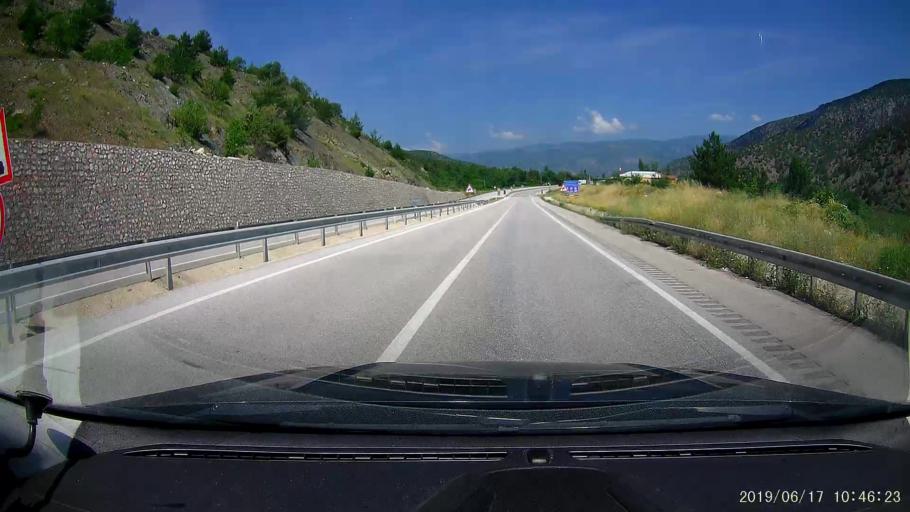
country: TR
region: Corum
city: Hacihamza
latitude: 41.0671
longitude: 34.4629
